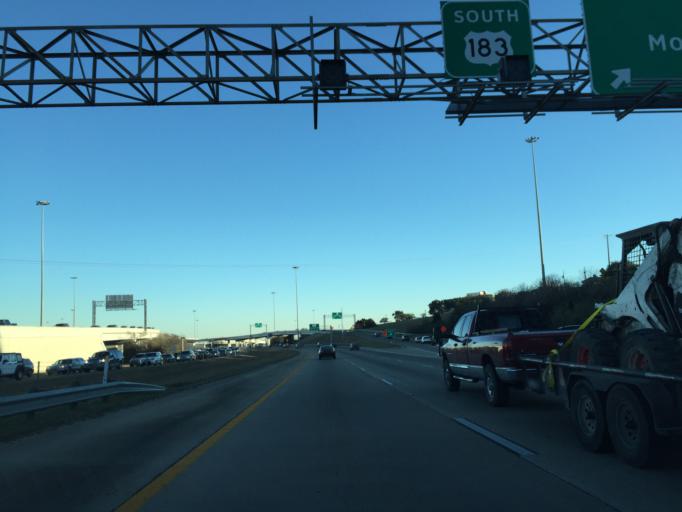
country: US
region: Texas
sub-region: Williamson County
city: Jollyville
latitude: 30.3843
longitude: -97.7426
